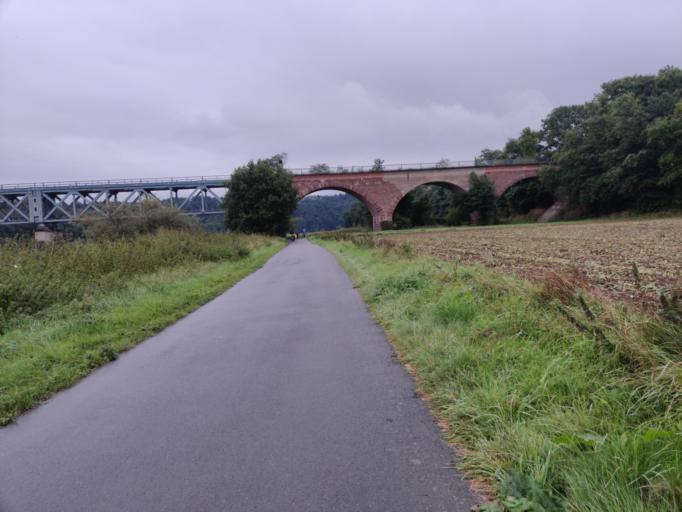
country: DE
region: Lower Saxony
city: Boffzen
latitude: 51.7364
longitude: 9.3805
